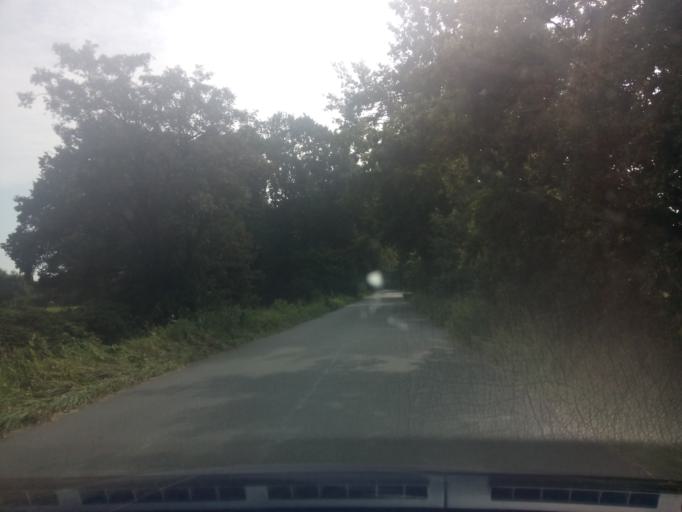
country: DE
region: Lower Saxony
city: Osterholz-Scharmbeck
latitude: 53.2434
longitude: 8.7620
